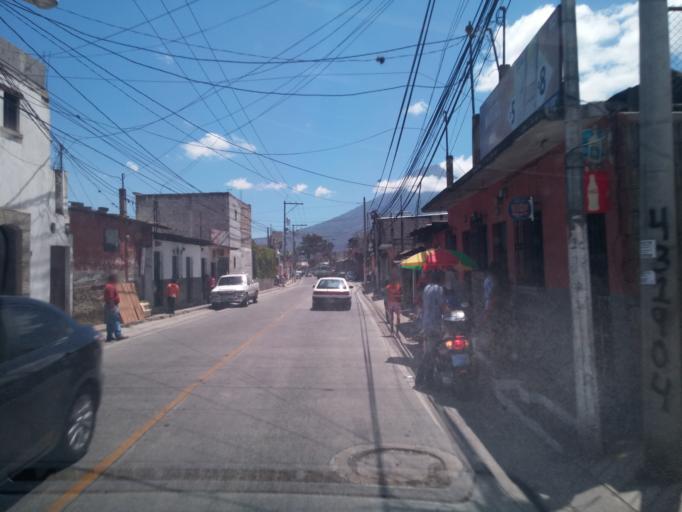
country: GT
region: Sacatepequez
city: Jocotenango
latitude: 14.5827
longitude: -90.7444
